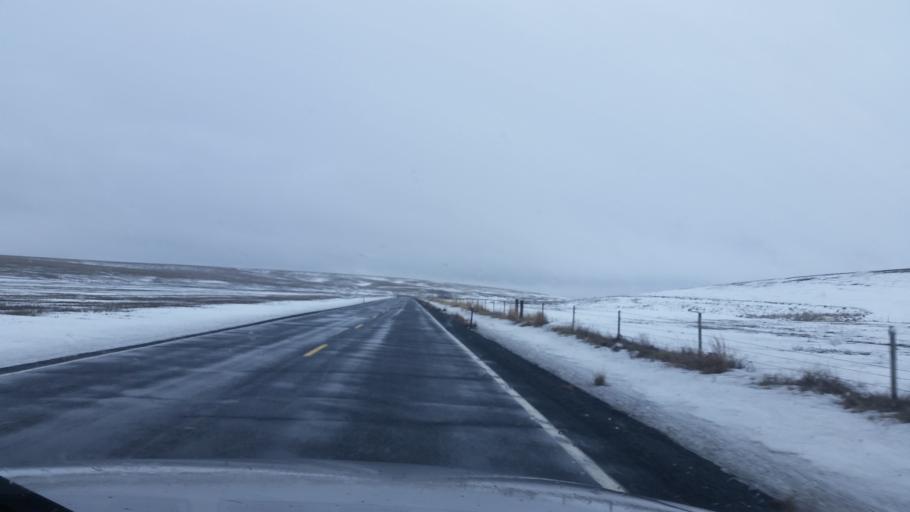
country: US
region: Washington
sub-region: Lincoln County
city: Davenport
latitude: 47.3962
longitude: -118.1545
